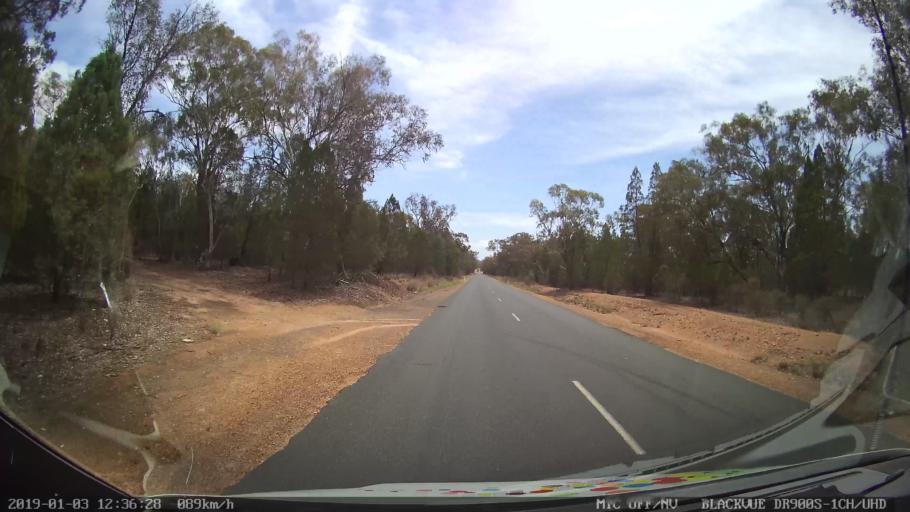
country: AU
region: New South Wales
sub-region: Weddin
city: Grenfell
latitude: -33.8546
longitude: 148.1770
